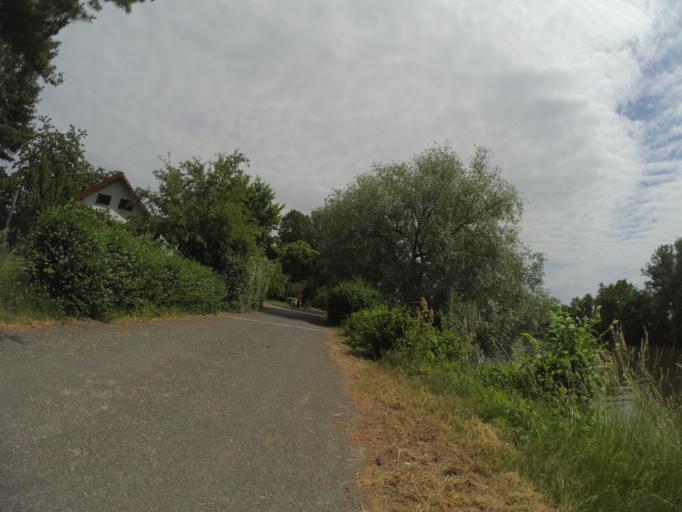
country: CZ
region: Central Bohemia
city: Prerov nad Labem
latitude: 50.1712
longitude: 14.8793
